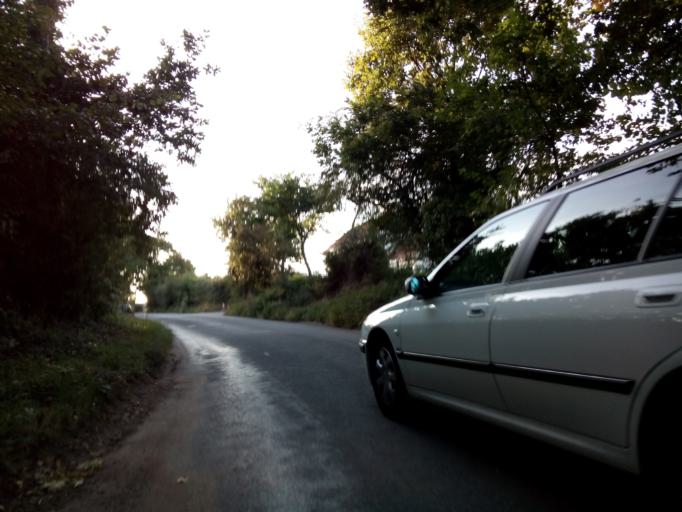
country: GB
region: England
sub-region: Suffolk
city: Bramford
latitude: 52.0313
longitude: 1.0863
